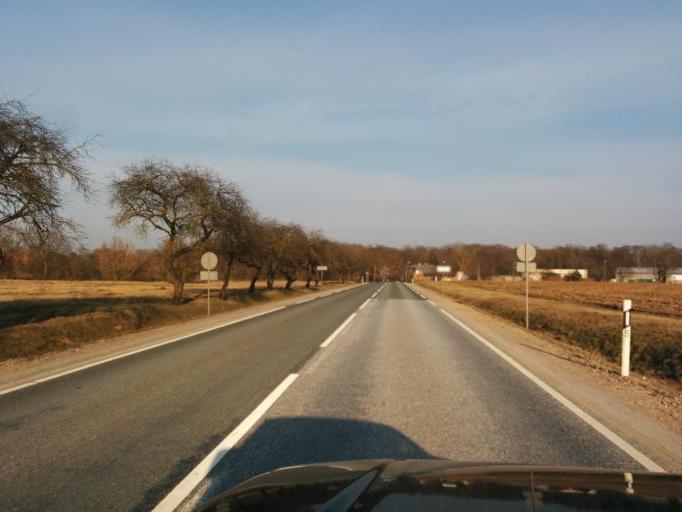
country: LV
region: Lecava
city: Iecava
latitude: 56.5937
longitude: 24.1873
